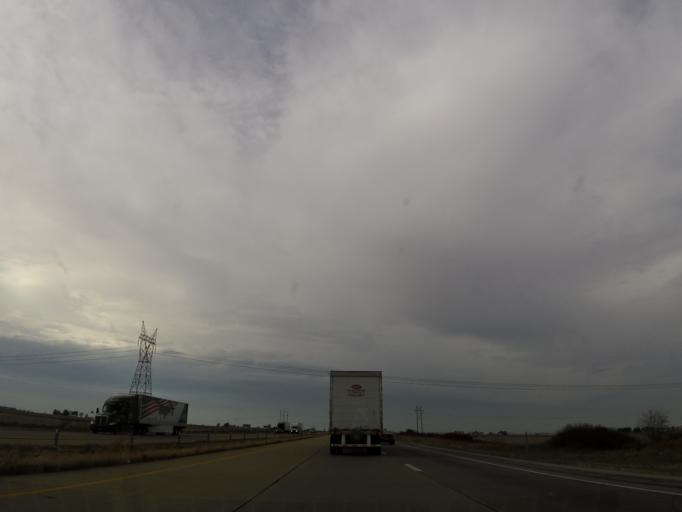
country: US
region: Iowa
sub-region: Scott County
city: Walcott
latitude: 41.6038
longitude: -90.6913
